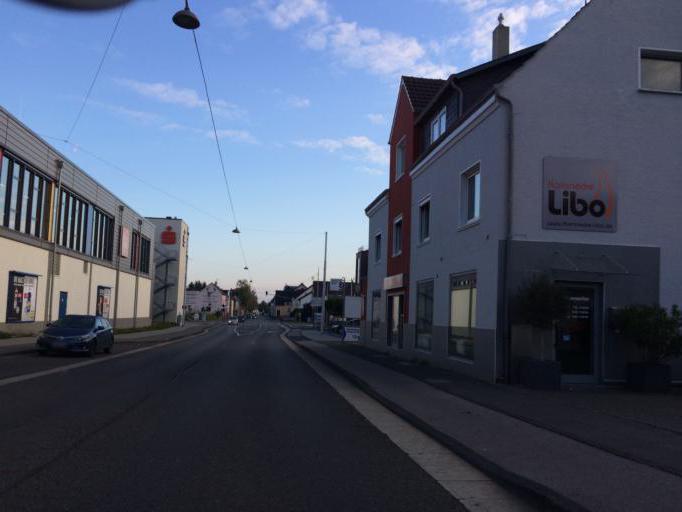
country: DE
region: North Rhine-Westphalia
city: Sankt Augustin
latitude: 50.7789
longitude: 7.1911
